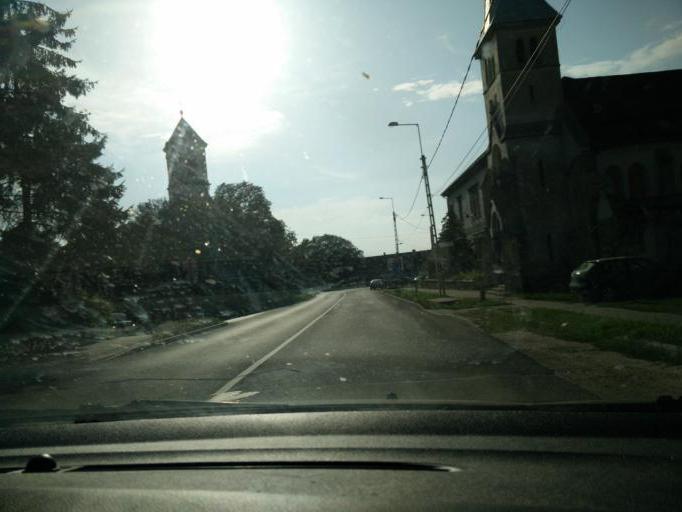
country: HU
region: Pest
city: Piliscsaba
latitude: 47.6321
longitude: 18.8275
